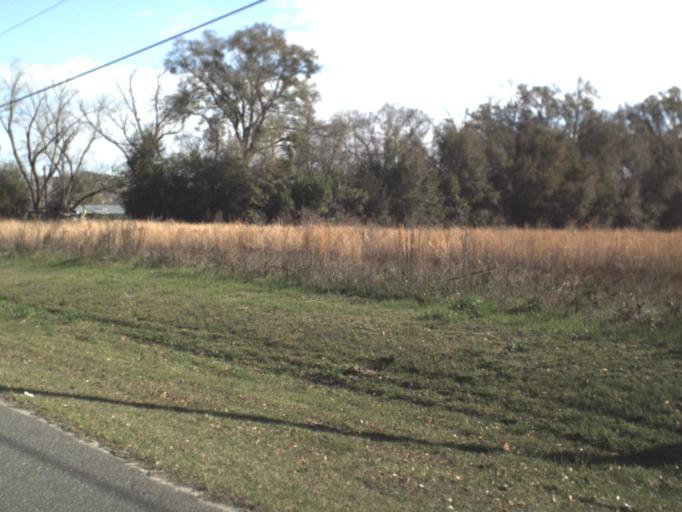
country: US
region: Florida
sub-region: Jackson County
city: Malone
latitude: 30.8944
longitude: -85.1611
